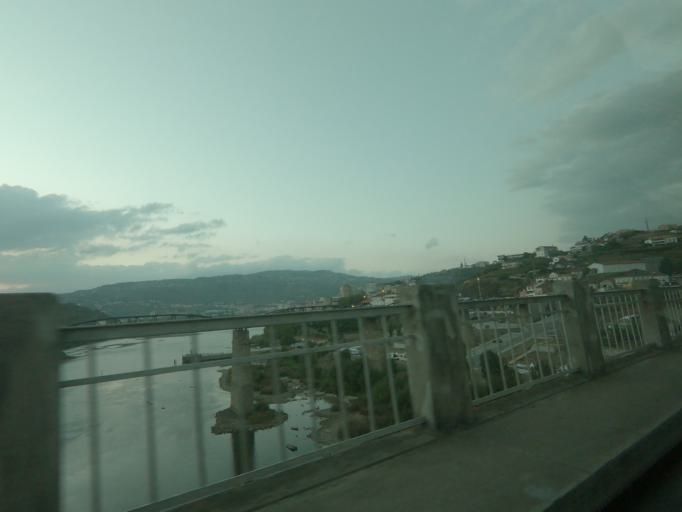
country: PT
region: Vila Real
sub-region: Peso da Regua
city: Peso da Regua
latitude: 41.1543
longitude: -7.7803
